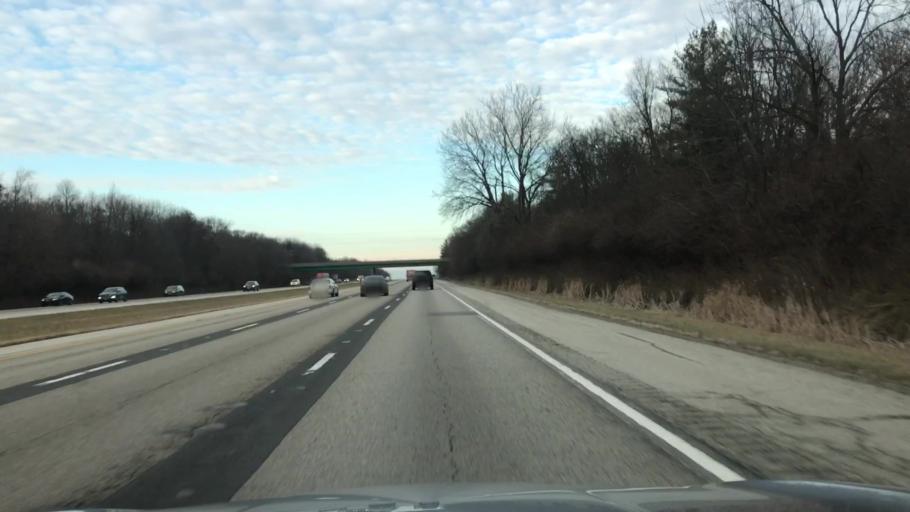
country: US
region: Illinois
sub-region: Logan County
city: Lincoln
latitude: 40.1442
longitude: -89.4170
